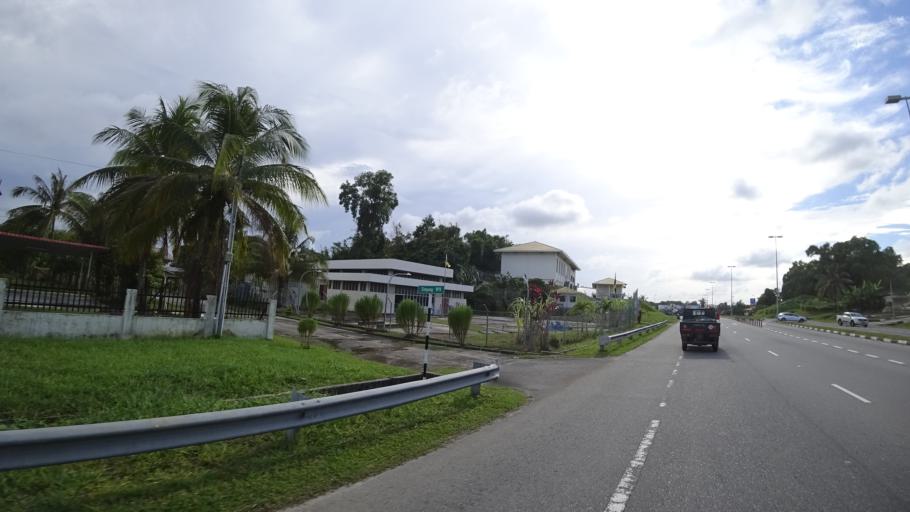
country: BN
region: Brunei and Muara
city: Bandar Seri Begawan
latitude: 4.8782
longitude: 114.8623
